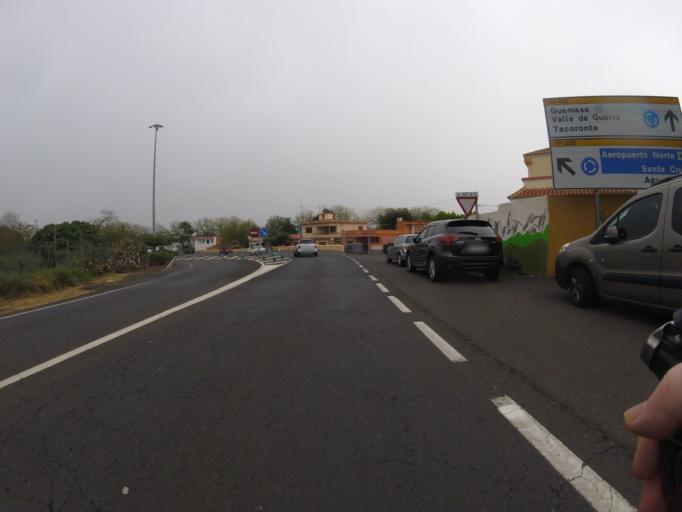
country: ES
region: Canary Islands
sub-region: Provincia de Santa Cruz de Tenerife
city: Tacoronte
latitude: 28.4921
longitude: -16.3728
